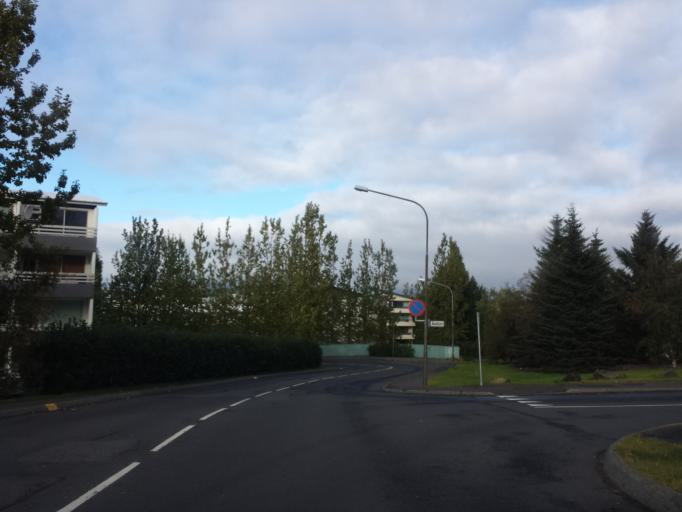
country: IS
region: Capital Region
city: Reykjavik
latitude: 64.1144
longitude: -21.8750
